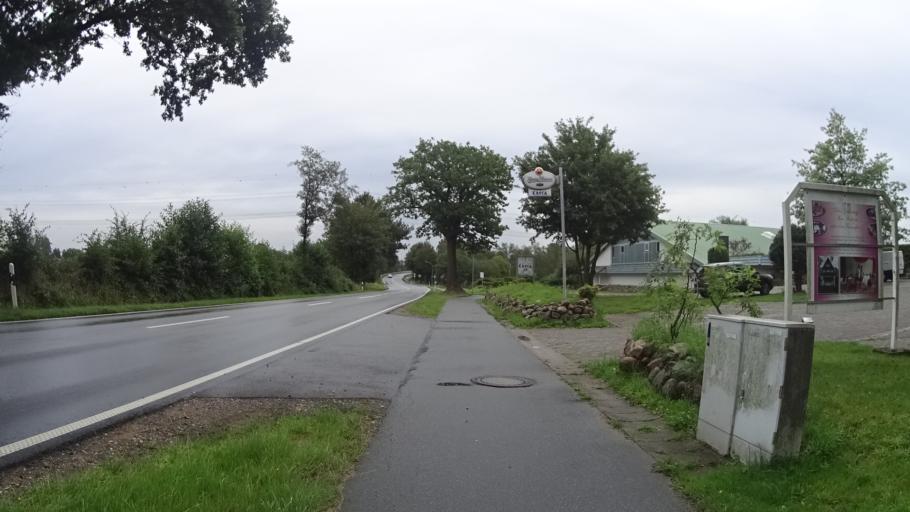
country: DE
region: Schleswig-Holstein
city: Alveslohe
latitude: 53.7890
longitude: 9.9318
